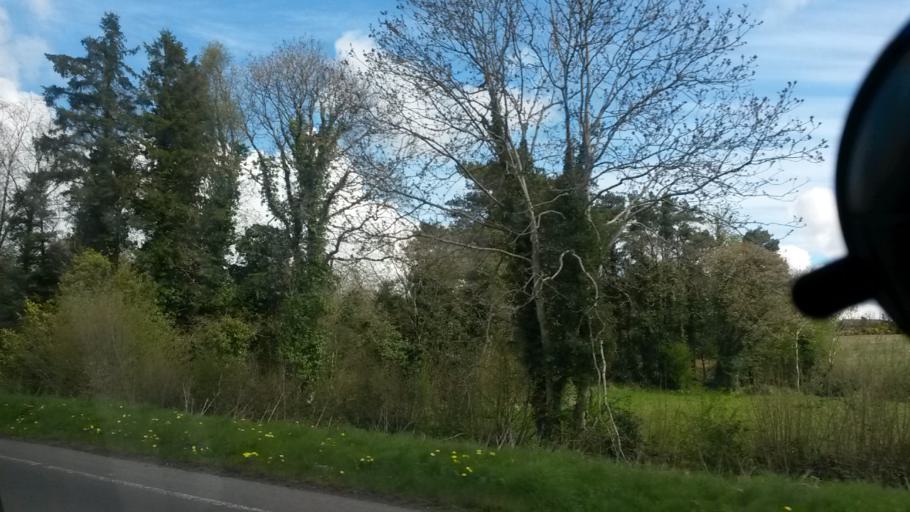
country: IE
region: Ulster
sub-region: An Cabhan
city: Ballyconnell
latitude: 54.1524
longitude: -7.5246
